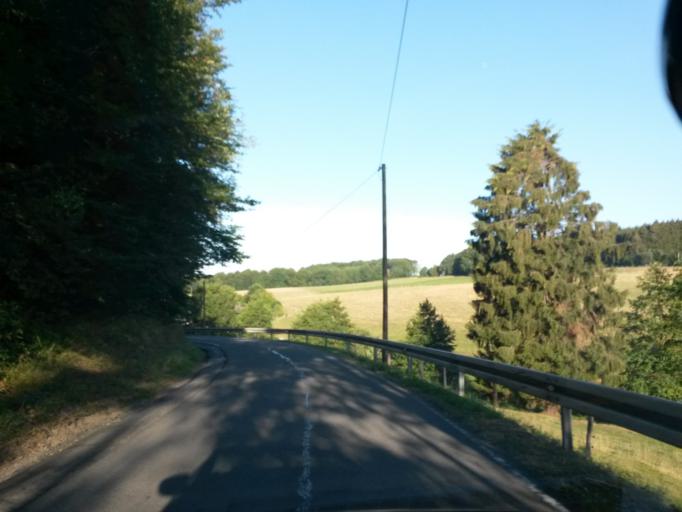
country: DE
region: North Rhine-Westphalia
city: Wipperfurth
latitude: 51.0832
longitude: 7.3985
